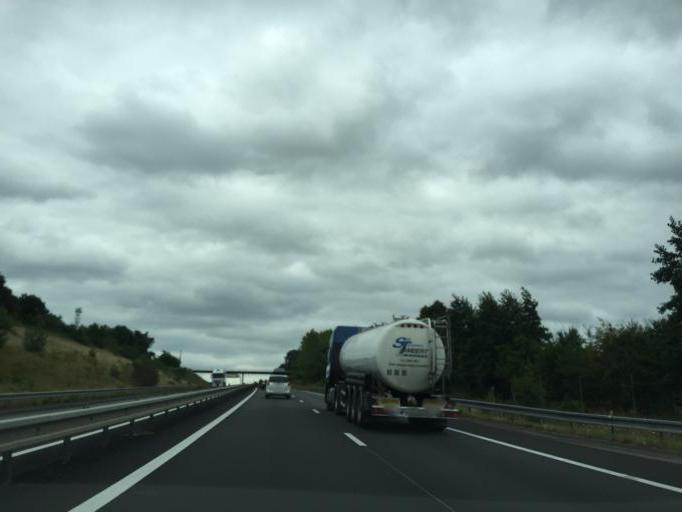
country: FR
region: Pays de la Loire
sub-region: Departement de la Sarthe
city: Change
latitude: 48.0217
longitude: 0.2924
